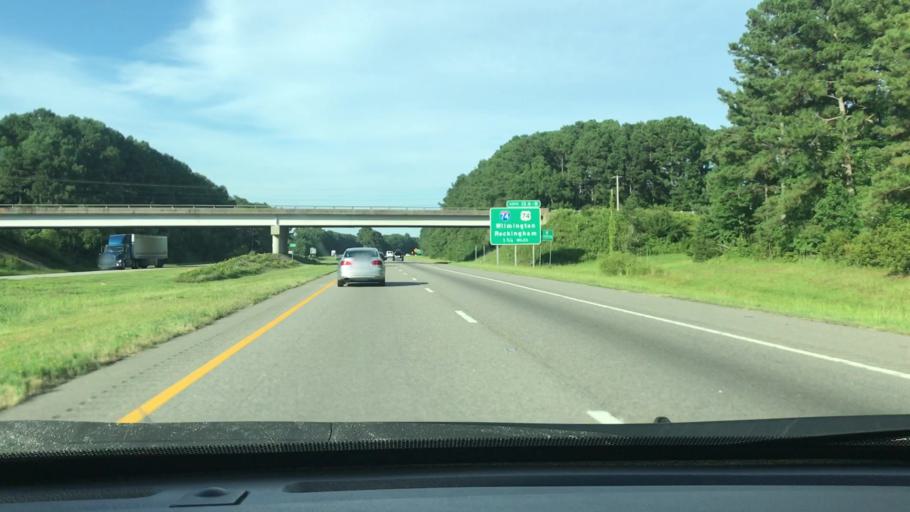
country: US
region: North Carolina
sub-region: Robeson County
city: Fairmont
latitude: 34.5760
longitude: -79.1526
